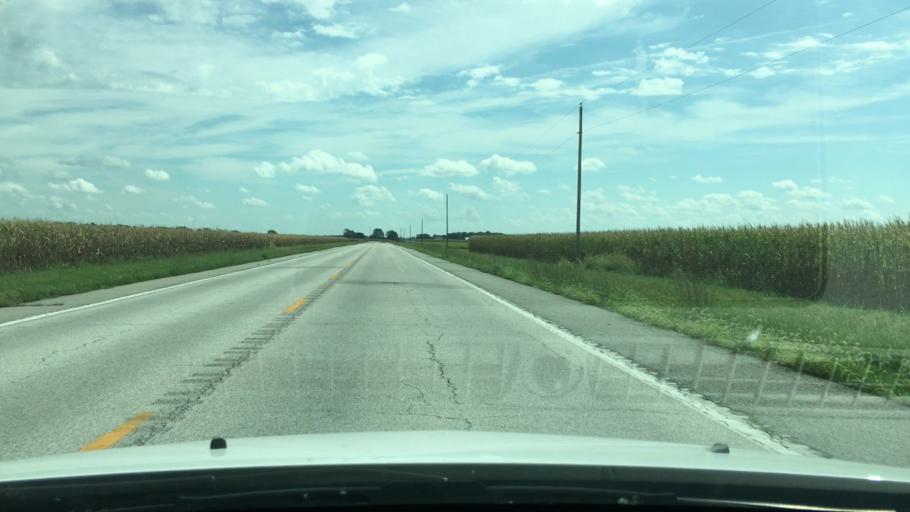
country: US
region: Missouri
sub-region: Audrain County
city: Vandalia
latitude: 39.2809
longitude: -91.6318
